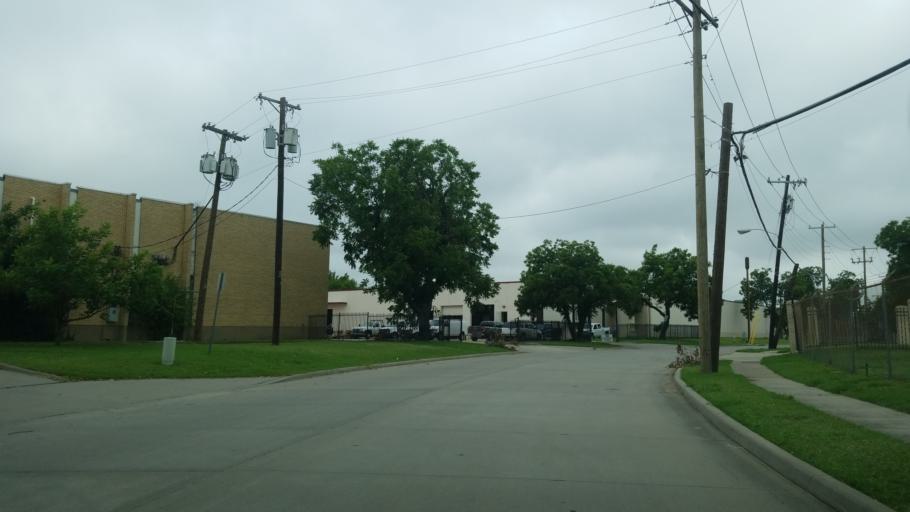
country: US
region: Texas
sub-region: Dallas County
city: Irving
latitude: 32.8349
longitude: -96.8798
